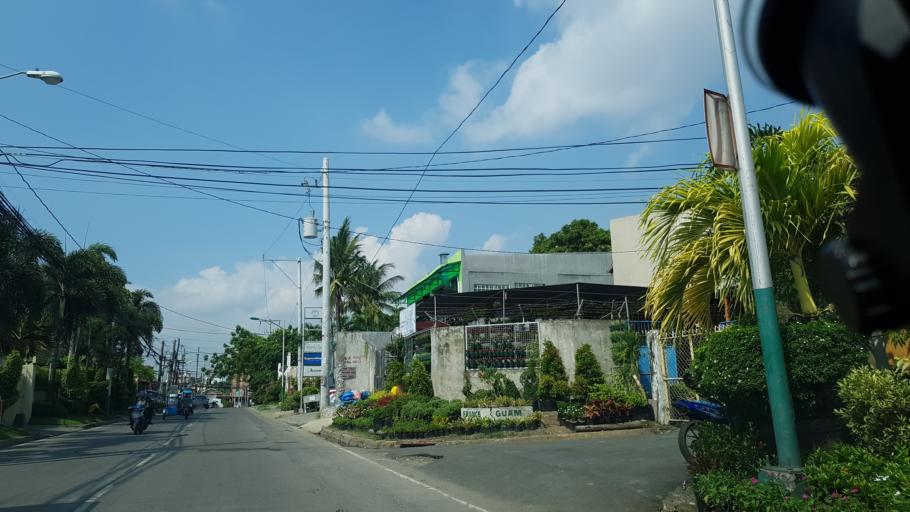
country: PH
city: Sambayanihan People's Village
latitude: 14.4829
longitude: 121.0310
